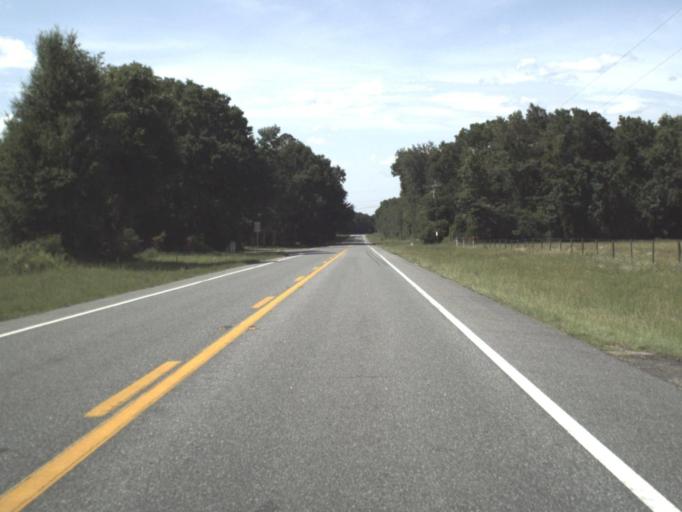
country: US
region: Florida
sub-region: Alachua County
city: High Springs
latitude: 29.8508
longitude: -82.7419
